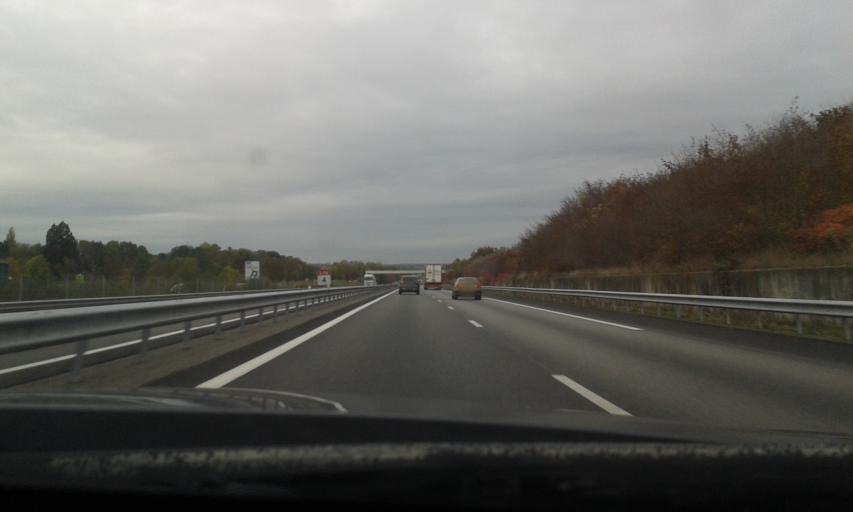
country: FR
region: Haute-Normandie
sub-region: Departement de l'Eure
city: Louviers
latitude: 49.2162
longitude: 1.1806
